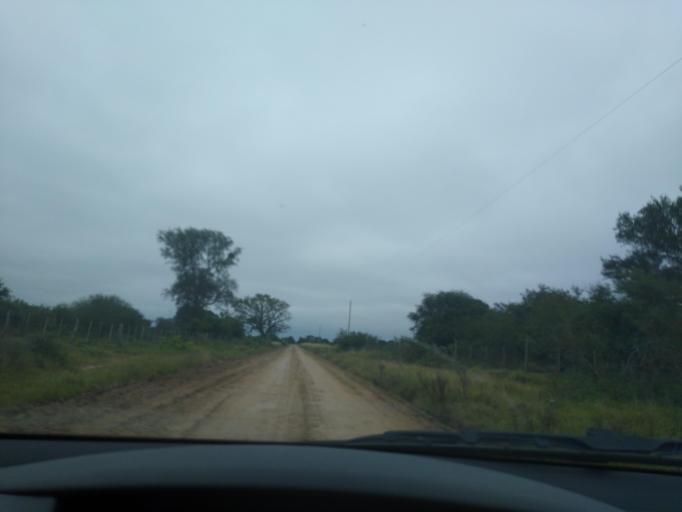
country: AR
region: Chaco
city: Colonia Benitez
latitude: -27.3650
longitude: -58.9542
